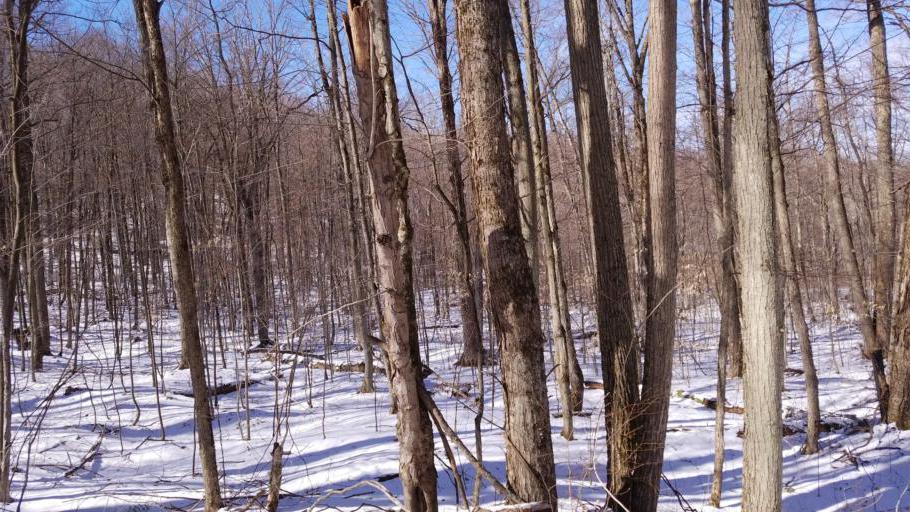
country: US
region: New York
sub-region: Allegany County
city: Wellsville
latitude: 42.0107
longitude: -77.9265
